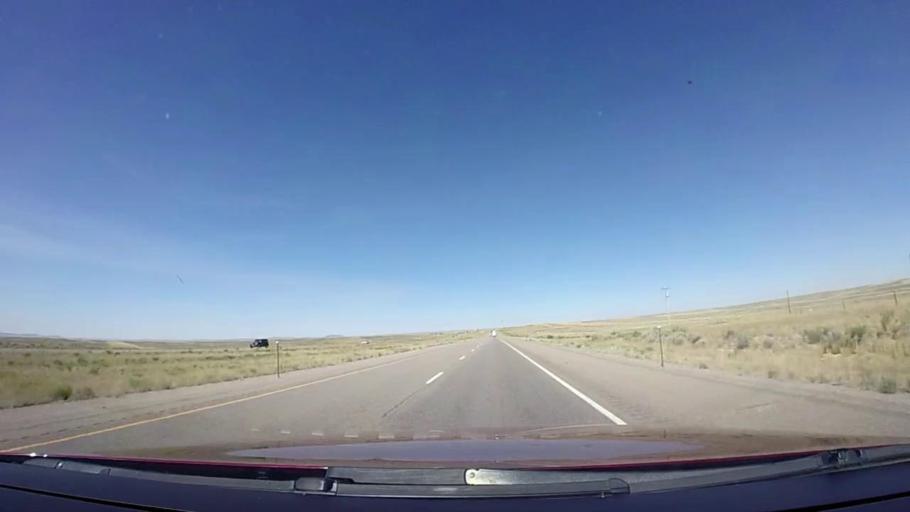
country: US
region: Wyoming
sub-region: Sweetwater County
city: Rock Springs
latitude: 41.6385
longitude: -108.4574
